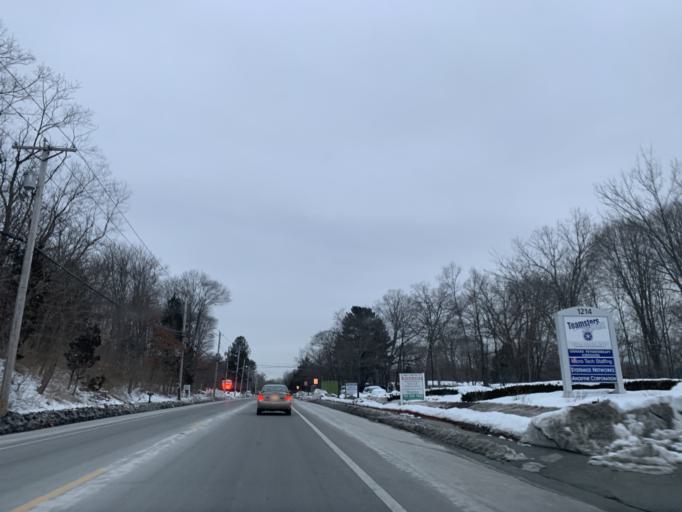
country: US
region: Massachusetts
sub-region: Norfolk County
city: Avon
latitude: 42.1050
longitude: -71.0689
